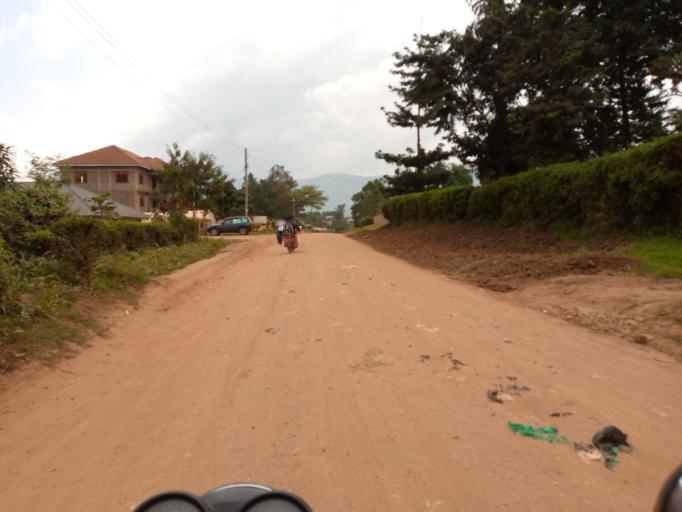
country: UG
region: Eastern Region
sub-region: Mbale District
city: Mbale
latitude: 1.0836
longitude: 34.1731
